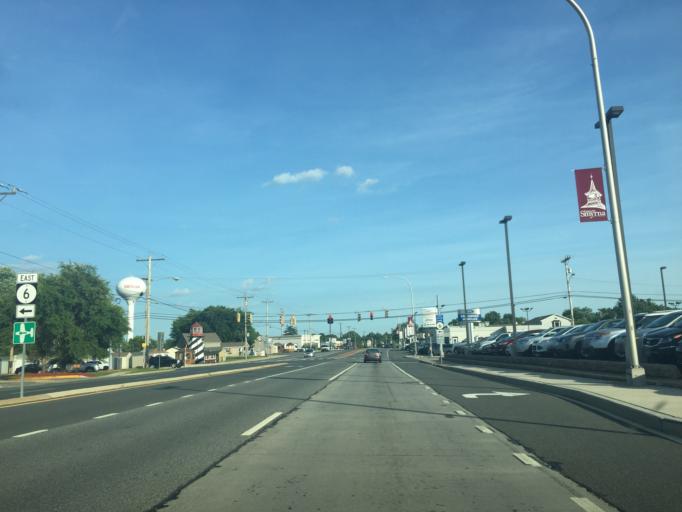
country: US
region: Delaware
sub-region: Kent County
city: Smyrna
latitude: 39.3032
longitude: -75.6044
